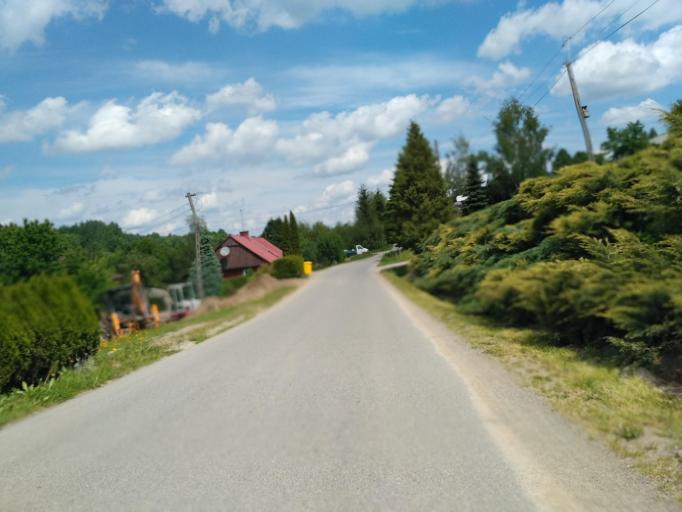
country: PL
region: Subcarpathian Voivodeship
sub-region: Powiat krosnienski
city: Dukla
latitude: 49.5708
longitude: 21.6164
